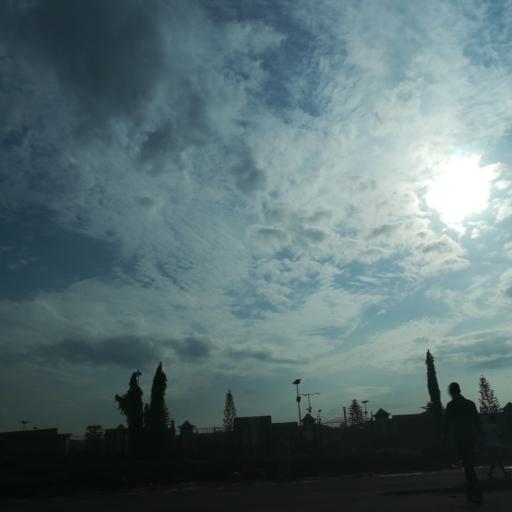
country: NG
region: Lagos
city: Oshodi
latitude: 6.5637
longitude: 3.3485
